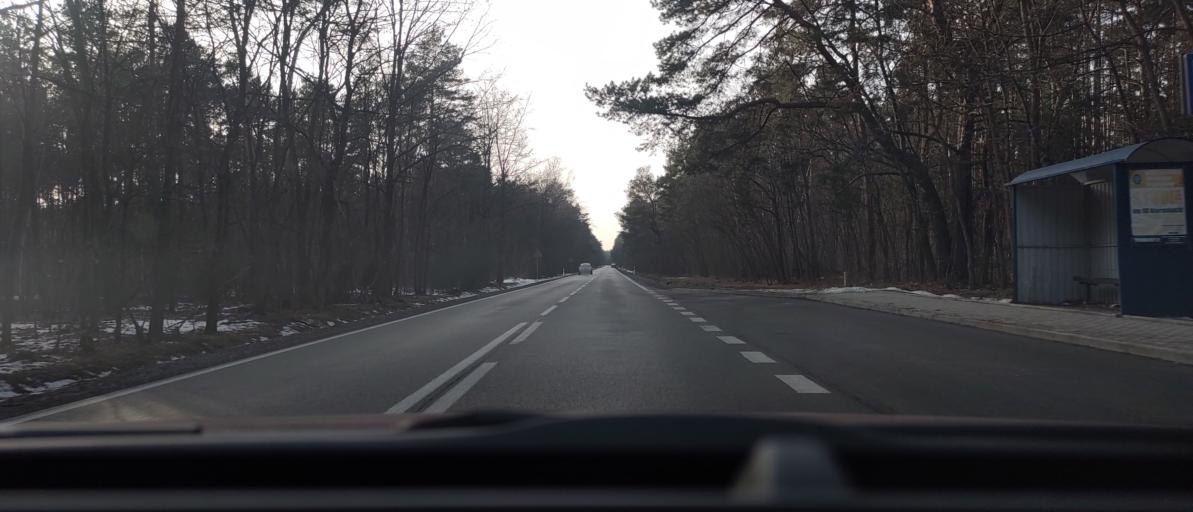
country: PL
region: Masovian Voivodeship
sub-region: Powiat bialobrzeski
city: Wysmierzyce
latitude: 51.6273
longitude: 20.8538
